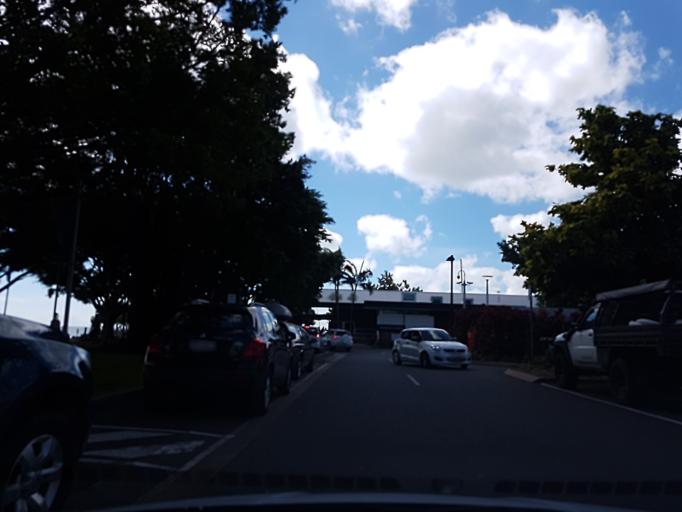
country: AU
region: Queensland
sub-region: Cairns
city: Cairns
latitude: -16.9189
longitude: 145.7801
